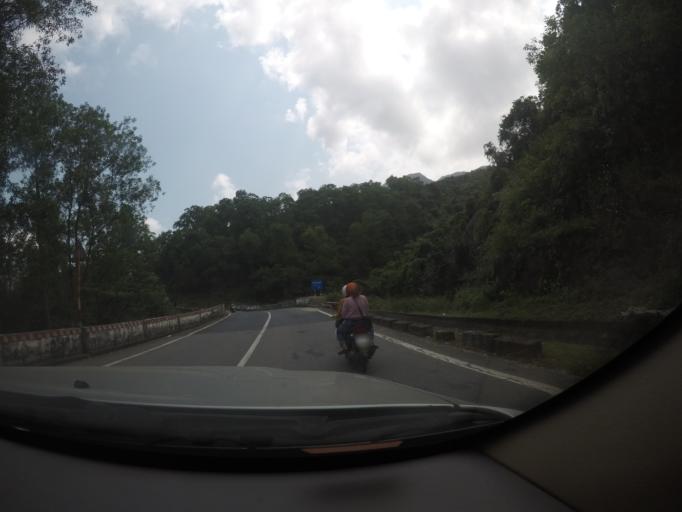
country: VN
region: Da Nang
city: Lien Chieu
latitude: 16.2061
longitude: 108.1100
